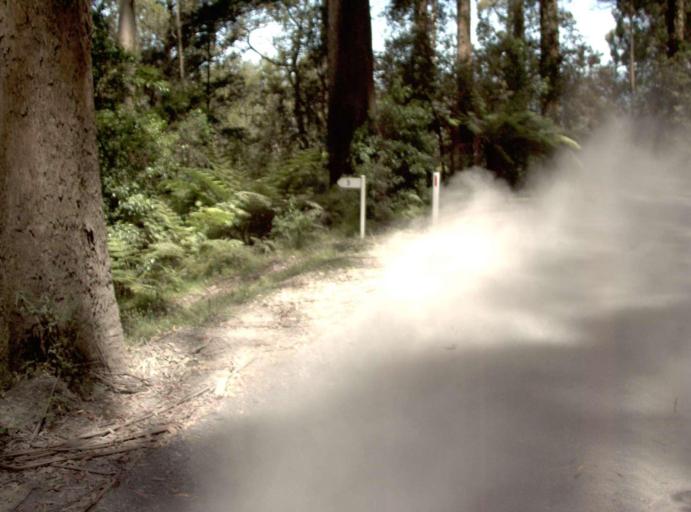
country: AU
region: Victoria
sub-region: Yarra Ranges
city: Millgrove
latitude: -37.7082
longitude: 145.7241
